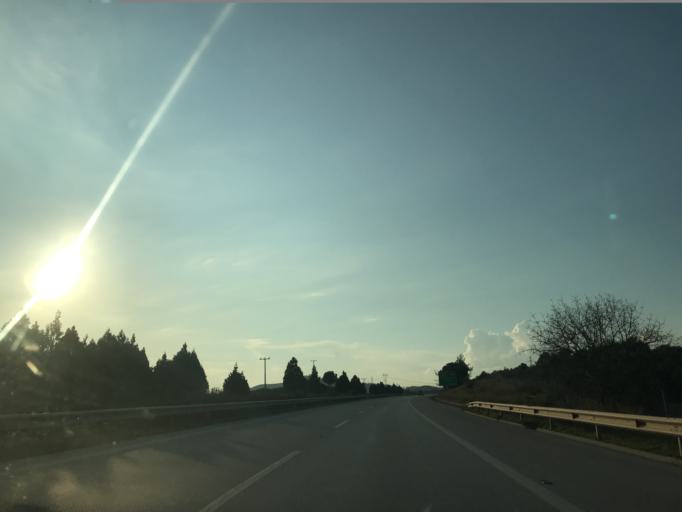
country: TR
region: Osmaniye
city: Toprakkale
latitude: 36.9671
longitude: 36.0406
